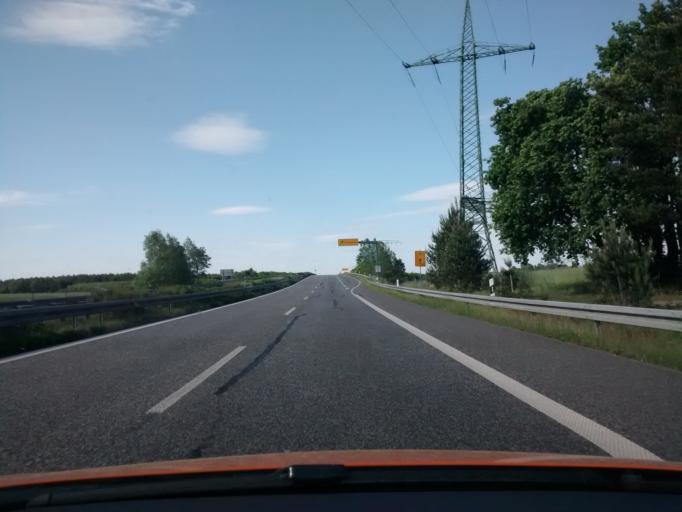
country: DE
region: Brandenburg
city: Ludwigsfelde
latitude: 52.2831
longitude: 13.2786
